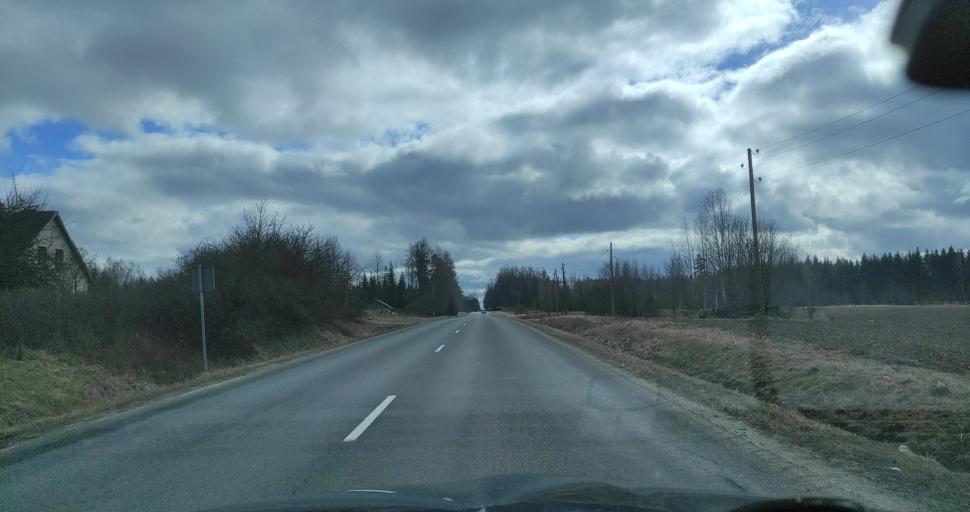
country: LV
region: Talsu Rajons
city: Stende
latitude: 57.1285
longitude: 22.5369
